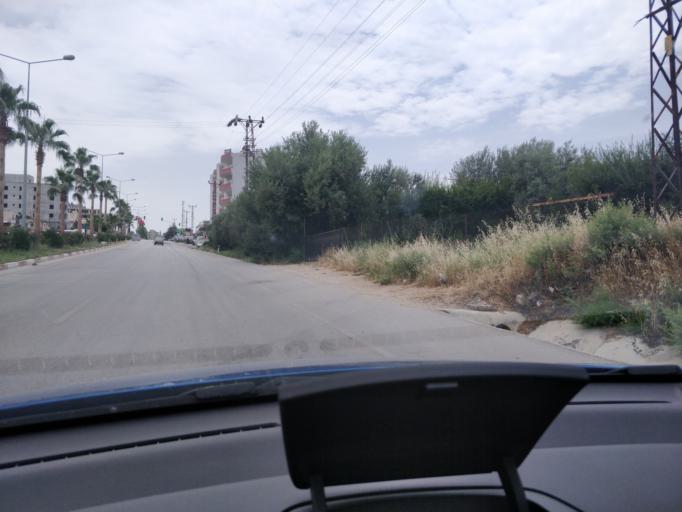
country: TR
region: Mersin
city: Mut
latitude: 36.6514
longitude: 33.4251
